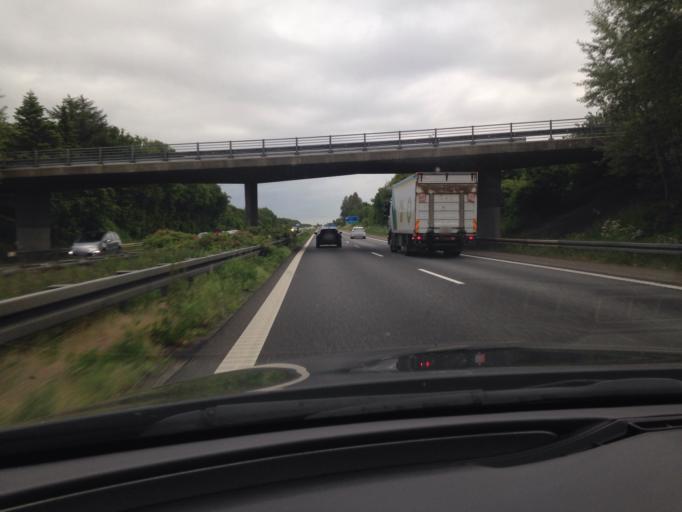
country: DK
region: South Denmark
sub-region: Fredericia Kommune
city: Taulov
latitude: 55.5422
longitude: 9.6112
